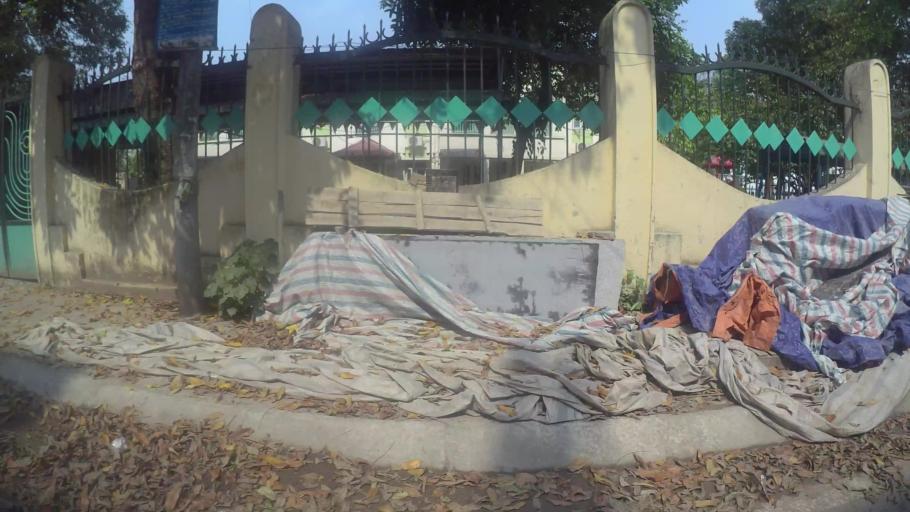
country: VN
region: Ha Noi
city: Tay Ho
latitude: 21.0866
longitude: 105.8106
